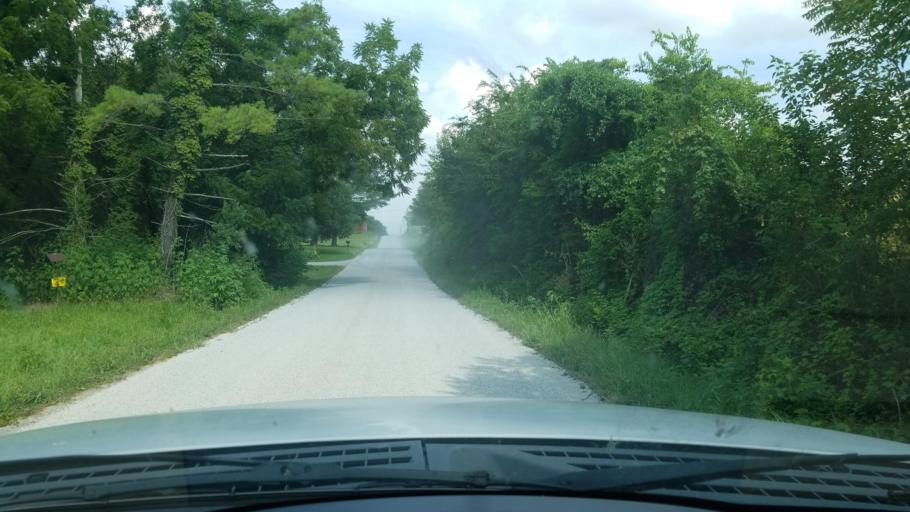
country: US
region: Illinois
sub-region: Saline County
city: Eldorado
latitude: 37.8345
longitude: -88.4374
